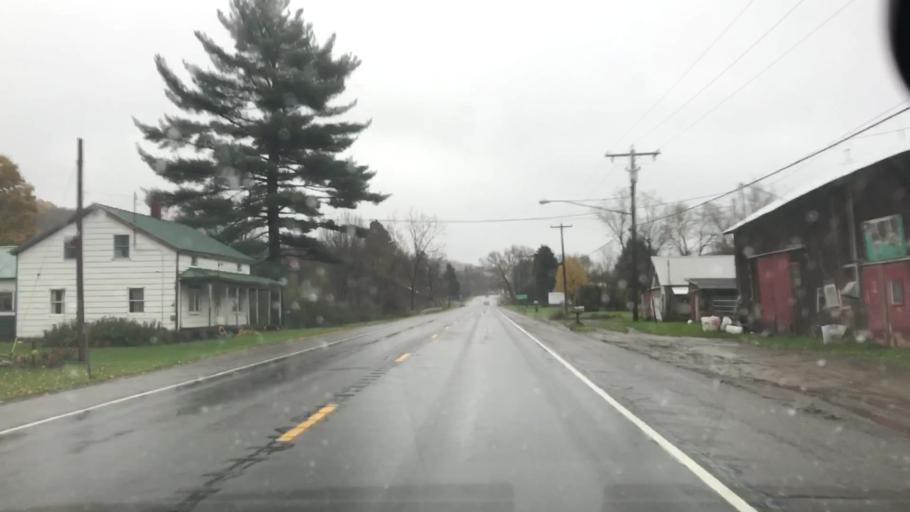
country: US
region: New York
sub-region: Erie County
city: Springville
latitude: 42.4014
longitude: -78.6825
